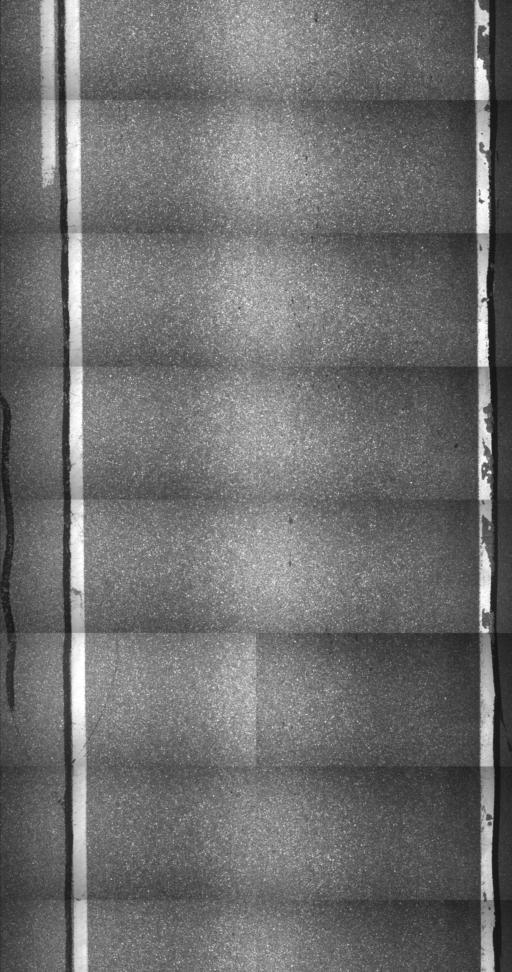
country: US
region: Vermont
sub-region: Chittenden County
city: Milton
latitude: 44.6408
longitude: -73.0158
